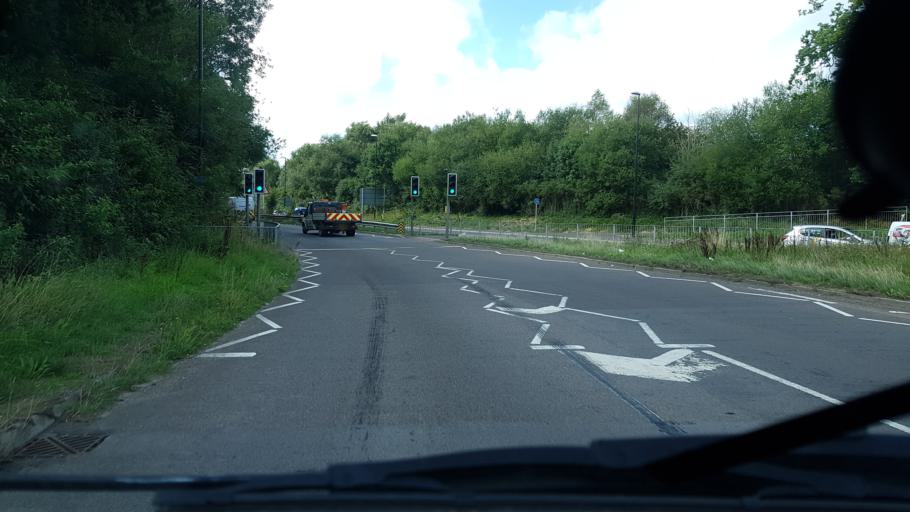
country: GB
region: England
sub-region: West Sussex
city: Broadfield
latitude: 51.0867
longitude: -0.1988
